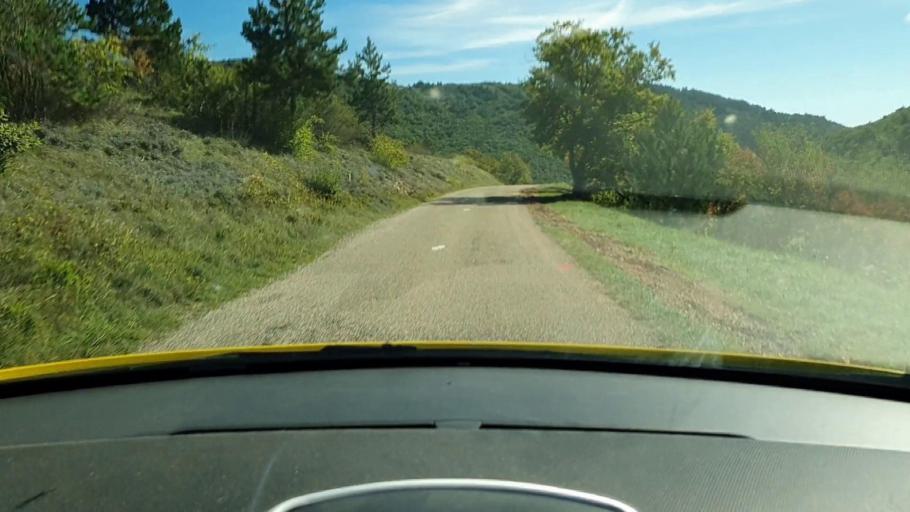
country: FR
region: Languedoc-Roussillon
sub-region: Departement du Gard
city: Aveze
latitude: 43.9613
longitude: 3.4317
